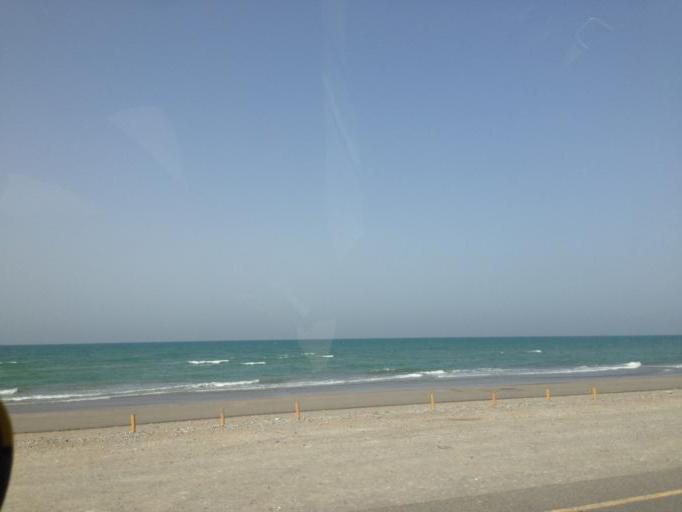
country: OM
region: Al Batinah
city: Barka'
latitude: 23.7239
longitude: 57.8487
